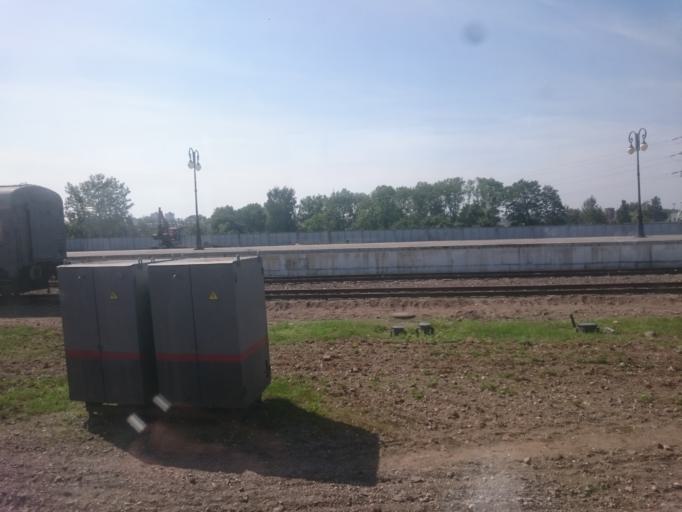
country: RU
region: Kaliningrad
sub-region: Gorod Kaliningrad
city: Kaliningrad
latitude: 54.6945
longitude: 20.4960
